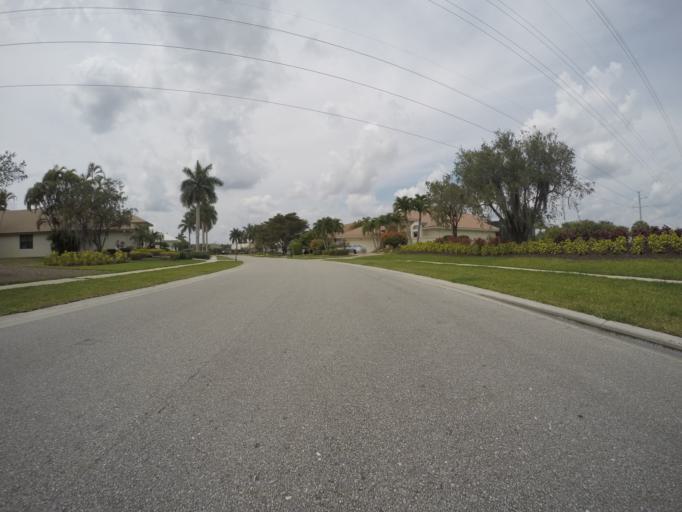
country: US
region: Florida
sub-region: Palm Beach County
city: Villages of Oriole
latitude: 26.4153
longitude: -80.2191
